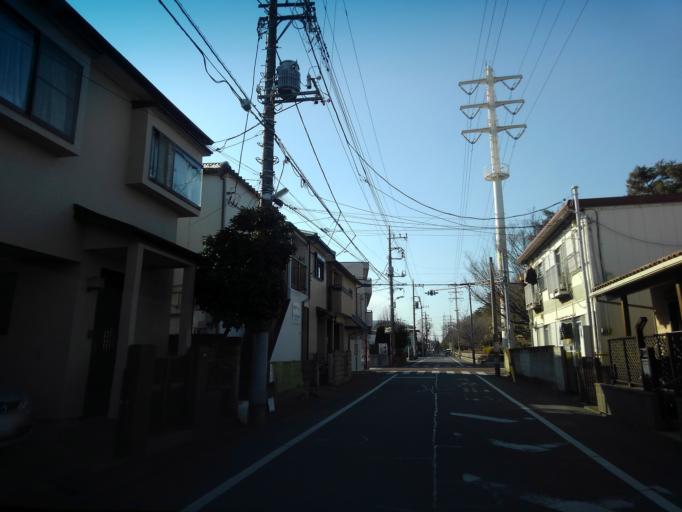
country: JP
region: Saitama
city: Tokorozawa
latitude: 35.8029
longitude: 139.4535
